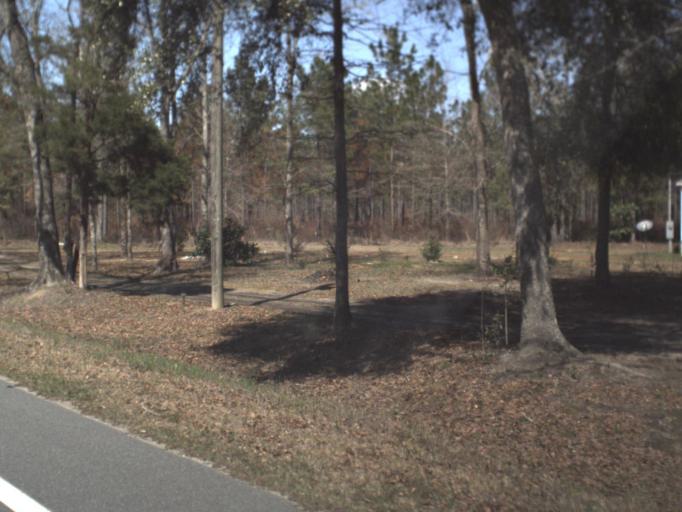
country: US
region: Florida
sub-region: Gadsden County
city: Gretna
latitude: 30.6669
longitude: -84.6983
